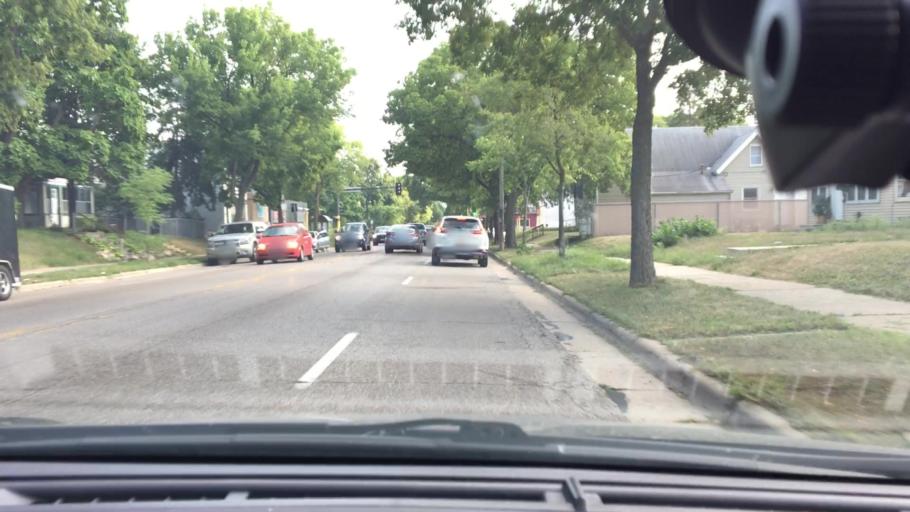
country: US
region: Minnesota
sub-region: Hennepin County
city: Minneapolis
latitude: 44.9405
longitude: -93.2475
